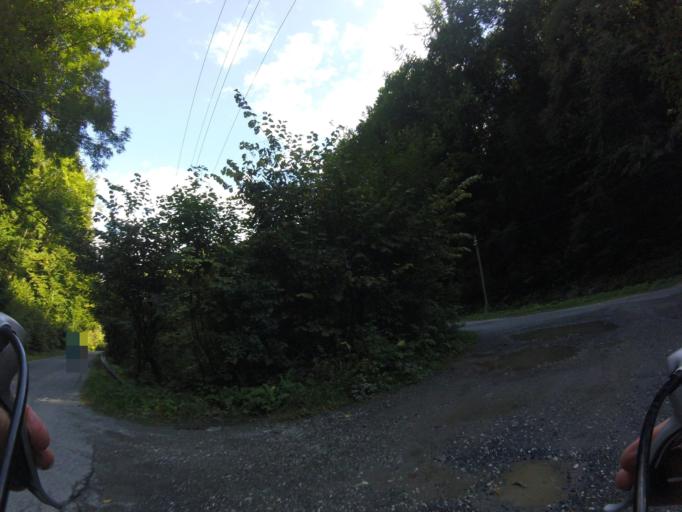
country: HU
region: Borsod-Abauj-Zemplen
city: Kazincbarcika
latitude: 48.1136
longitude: 20.5916
